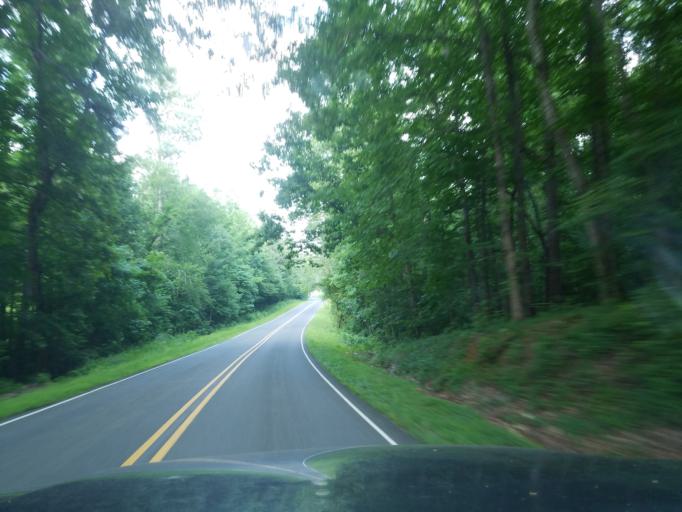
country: US
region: North Carolina
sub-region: Granville County
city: Butner
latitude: 36.2018
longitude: -78.8561
